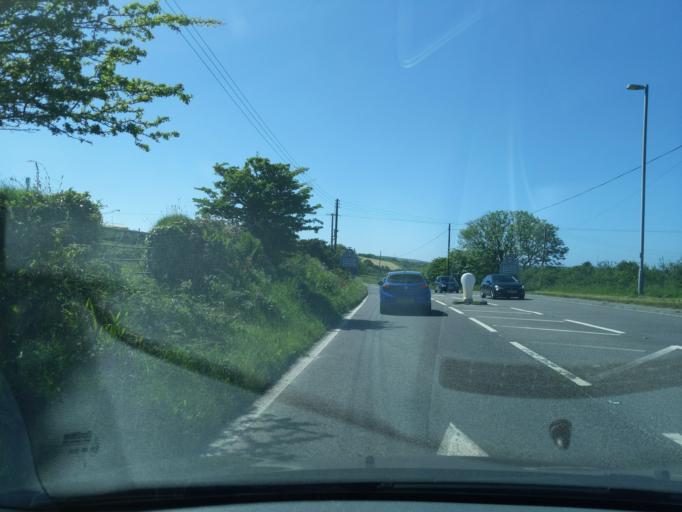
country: GB
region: England
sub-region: Cornwall
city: Penryn
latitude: 50.1649
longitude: -5.1628
